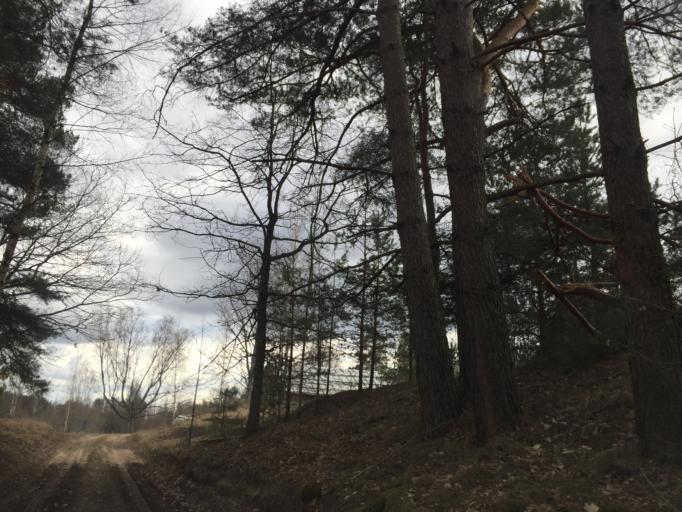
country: LV
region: Lielvarde
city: Lielvarde
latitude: 56.4897
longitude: 24.7799
